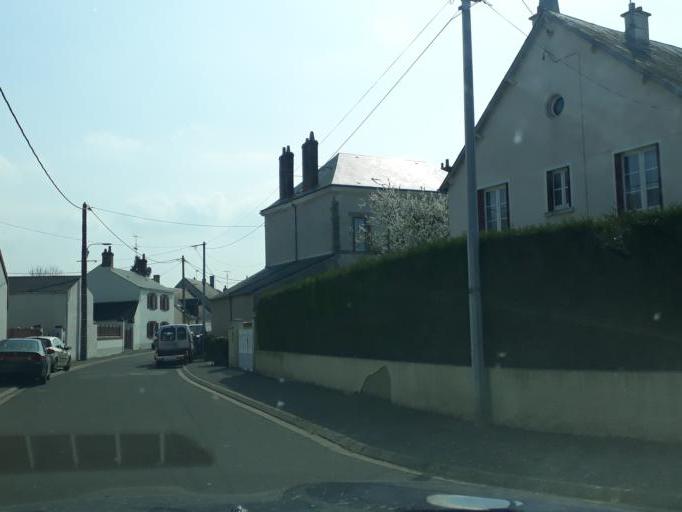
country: FR
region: Centre
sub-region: Departement du Loiret
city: Artenay
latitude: 48.0839
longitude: 1.8780
